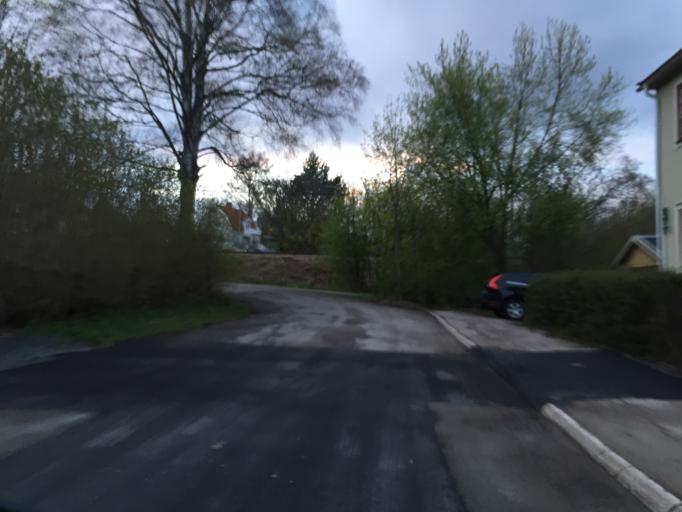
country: SE
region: Dalarna
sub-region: Ludvika Kommun
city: Ludvika
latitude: 60.1472
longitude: 15.1950
